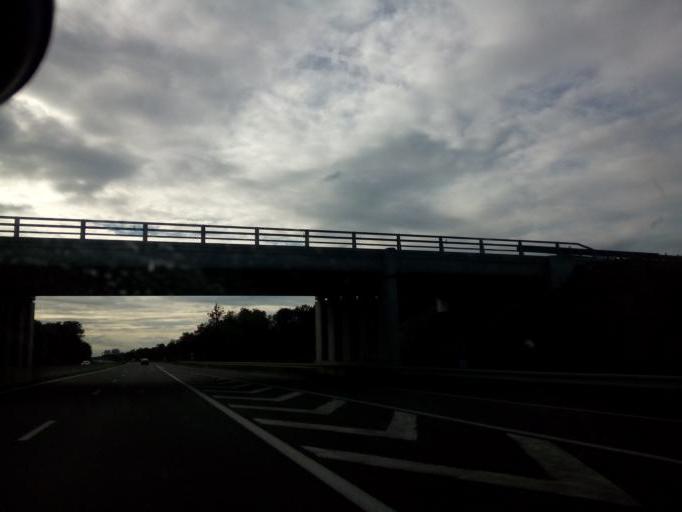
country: FR
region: Centre
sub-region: Departement d'Indre-et-Loire
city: Esvres
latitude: 47.3085
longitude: 0.8020
